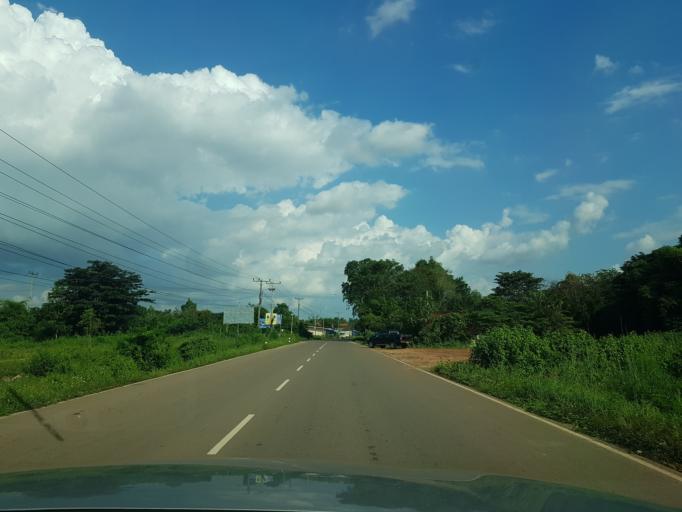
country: TH
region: Nong Khai
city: Pho Tak
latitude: 17.9795
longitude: 102.4617
